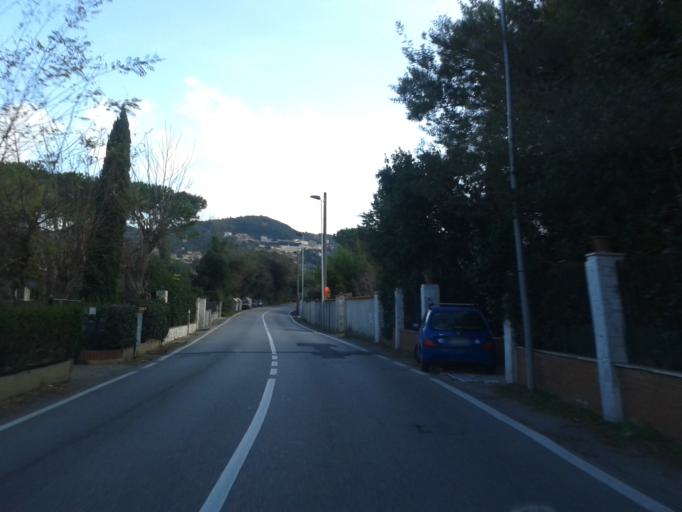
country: IT
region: Tuscany
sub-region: Provincia di Livorno
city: Livorno
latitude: 43.5033
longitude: 10.3388
